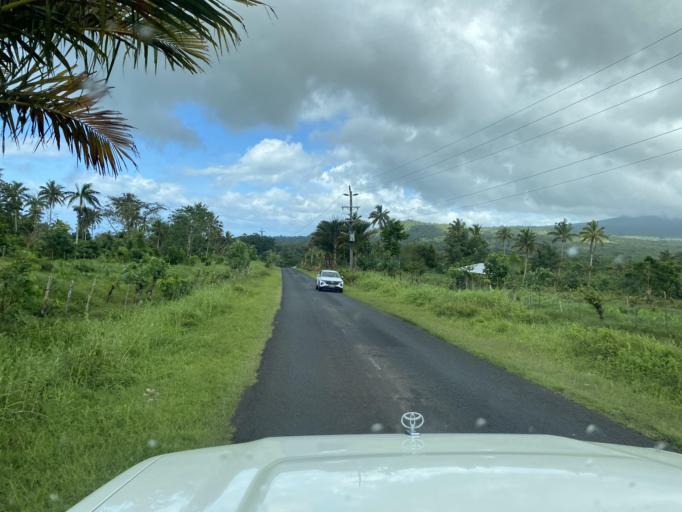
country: WS
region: Va`a-o-Fonoti
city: Samamea
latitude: -13.9769
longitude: -171.5853
